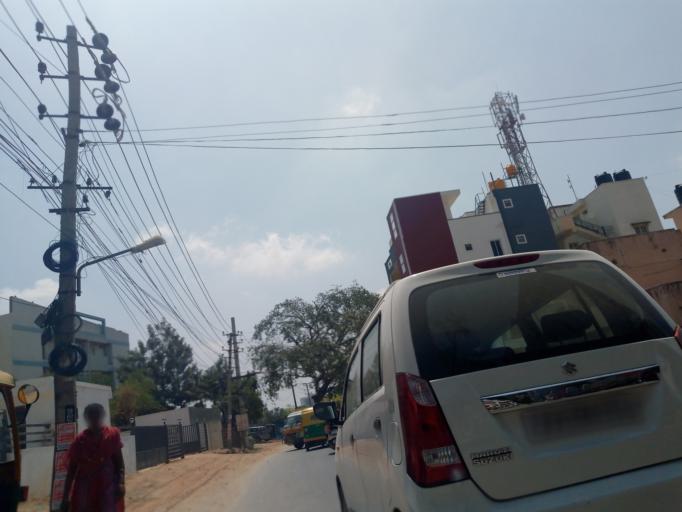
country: IN
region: Karnataka
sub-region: Bangalore Urban
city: Bangalore
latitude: 12.8946
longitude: 77.6528
